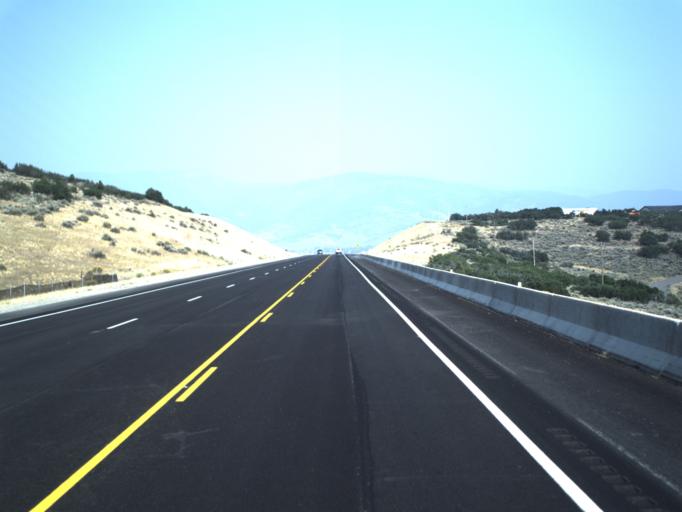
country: US
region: Utah
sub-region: Summit County
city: Kamas
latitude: 40.6349
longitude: -111.3431
